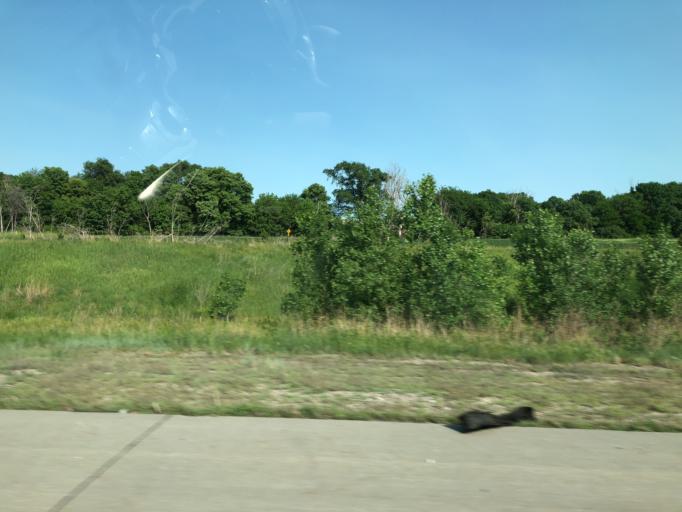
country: US
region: Nebraska
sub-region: Sarpy County
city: Gretna
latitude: 41.0735
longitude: -96.2838
